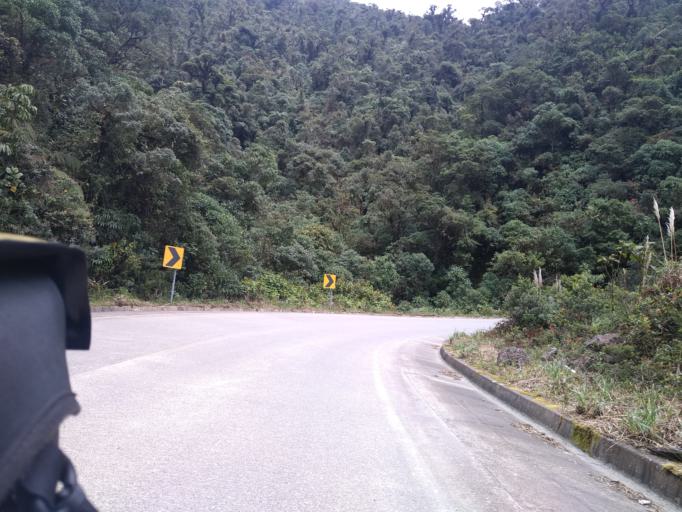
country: EC
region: Zamora-Chinchipe
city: Zamora
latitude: -4.4312
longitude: -79.1493
